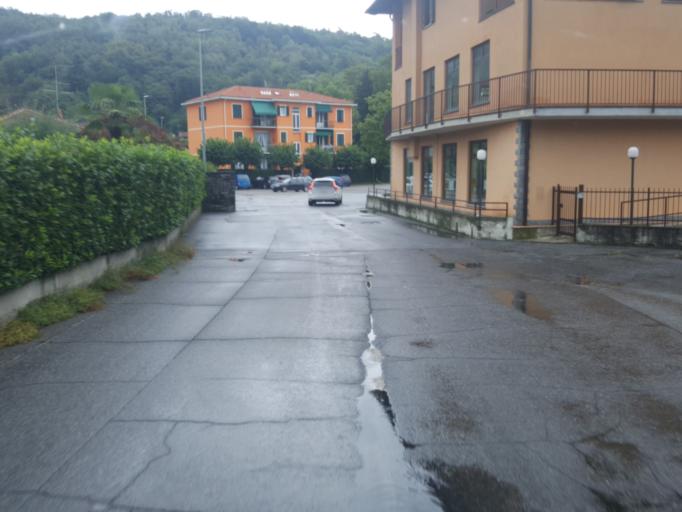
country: IT
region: Piedmont
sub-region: Provincia Verbano-Cusio-Ossola
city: Vignone
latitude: 45.9518
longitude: 8.5539
